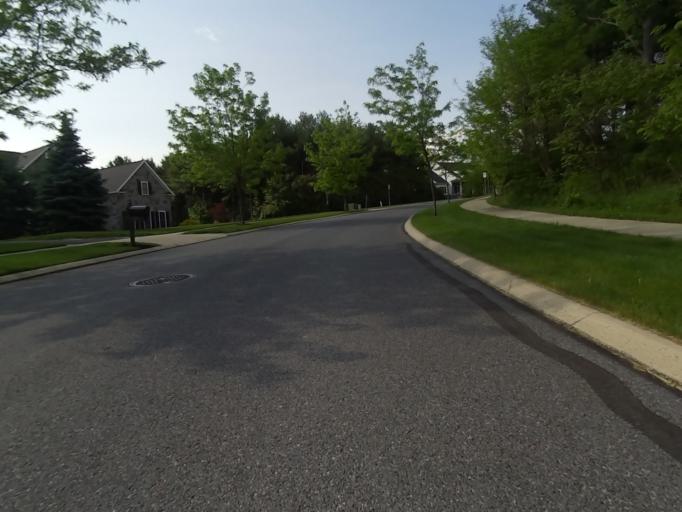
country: US
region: Pennsylvania
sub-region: Centre County
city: Houserville
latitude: 40.8211
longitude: -77.8208
